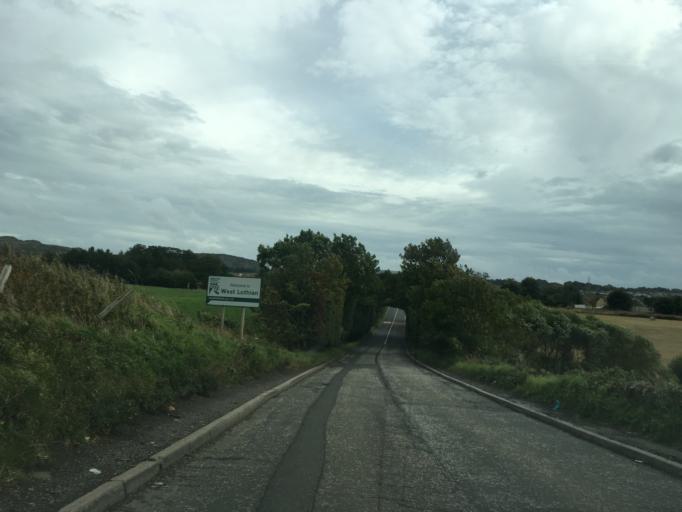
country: GB
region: Scotland
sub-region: West Lothian
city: Kirknewton
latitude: 55.9039
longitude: -3.4068
